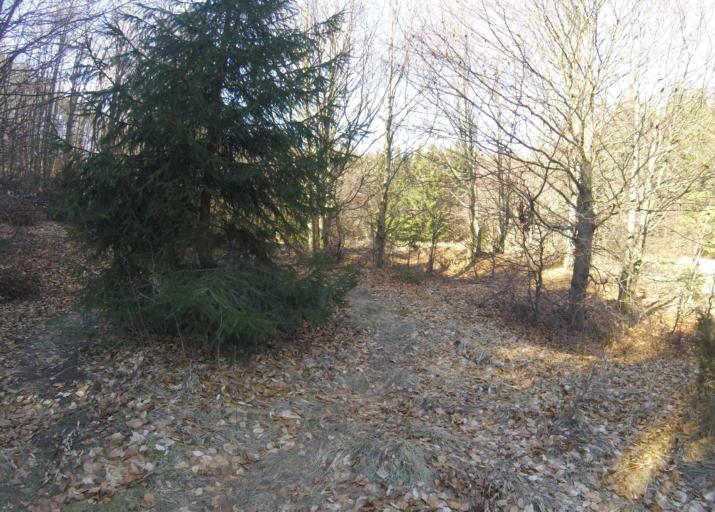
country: HU
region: Heves
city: Szilvasvarad
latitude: 48.0729
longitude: 20.4747
